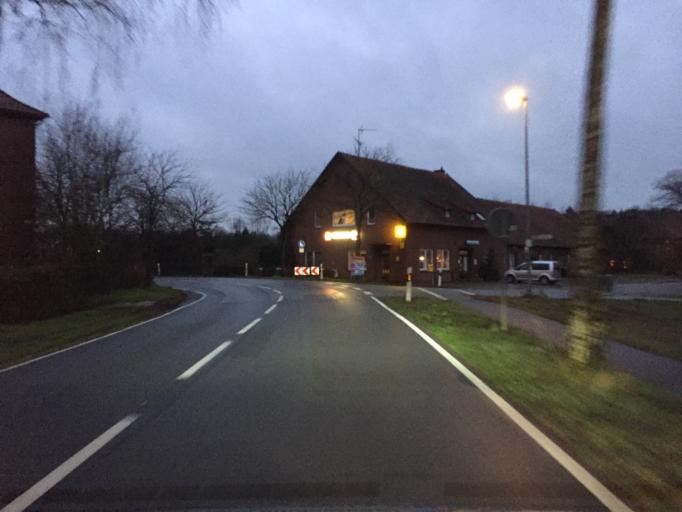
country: DE
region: Lower Saxony
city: Schwaforden
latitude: 52.7427
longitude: 8.8185
